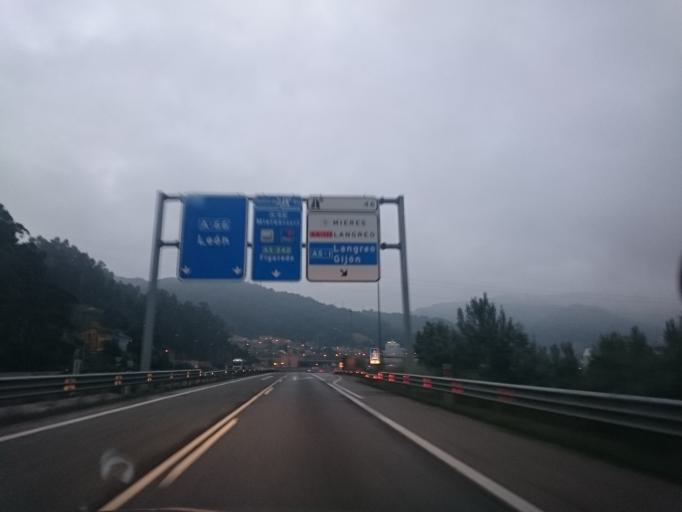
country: ES
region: Asturias
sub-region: Province of Asturias
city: Mieres
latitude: 43.2641
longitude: -5.7899
